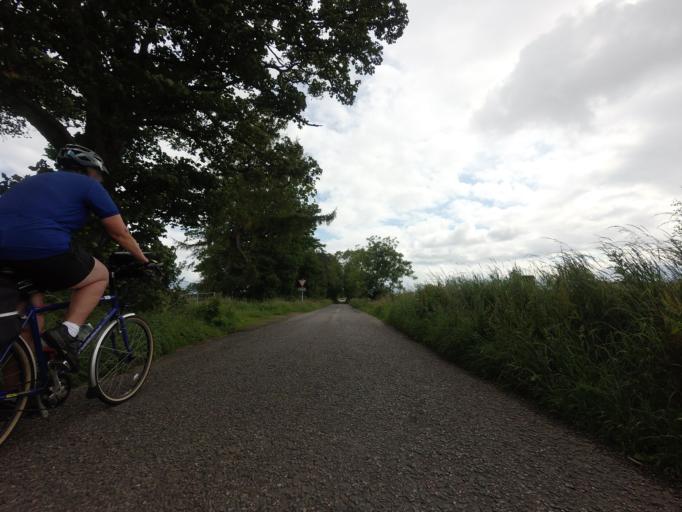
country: GB
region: Scotland
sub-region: Moray
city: Lhanbryd
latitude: 57.6458
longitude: -3.2532
